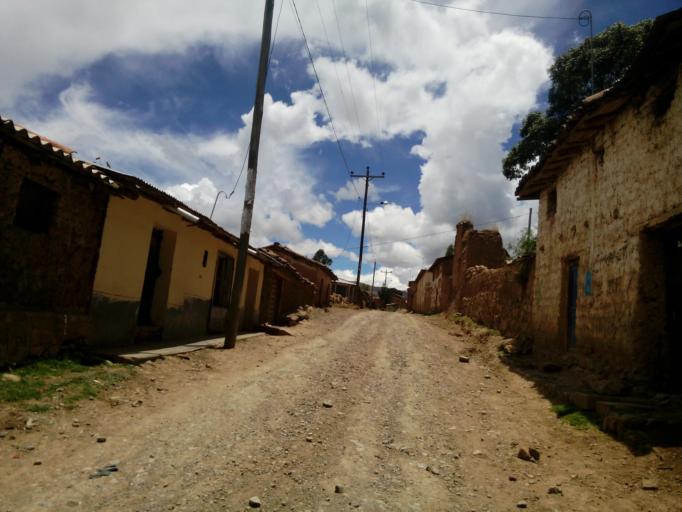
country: PE
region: Ayacucho
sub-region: Provincia de Victor Fajardo
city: Canaria
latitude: -13.8777
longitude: -73.9362
